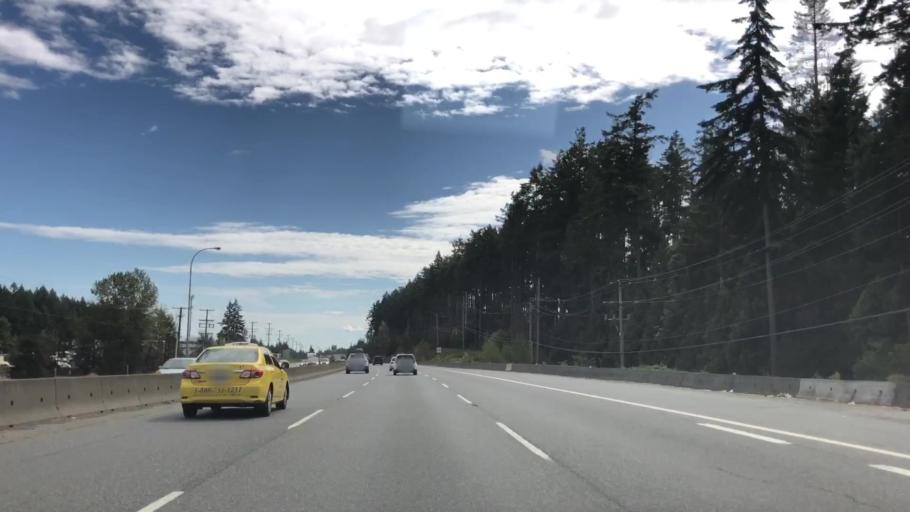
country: CA
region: British Columbia
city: Nanaimo
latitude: 49.1093
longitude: -123.9008
